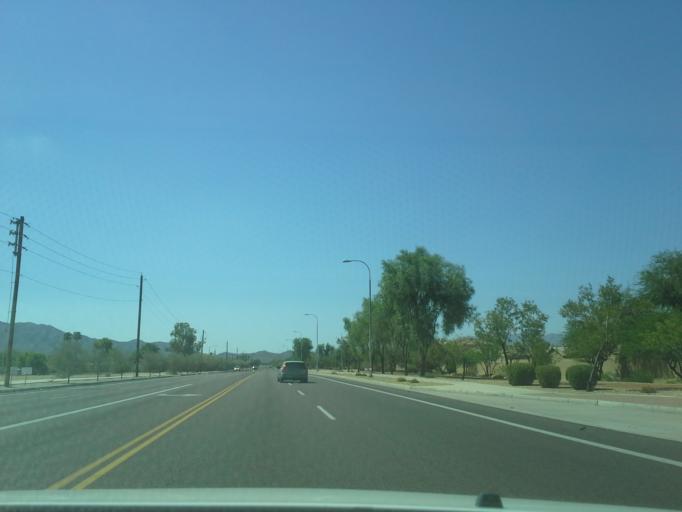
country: US
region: Arizona
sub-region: Maricopa County
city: Laveen
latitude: 33.3917
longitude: -112.1509
